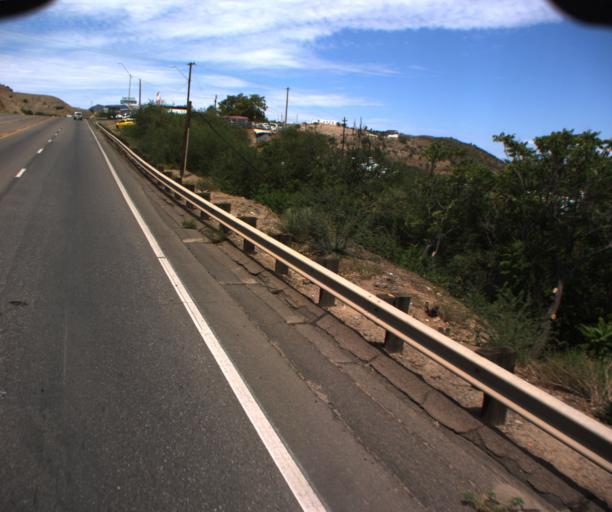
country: US
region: Arizona
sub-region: Gila County
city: Central Heights-Midland City
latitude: 33.4161
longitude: -110.8013
